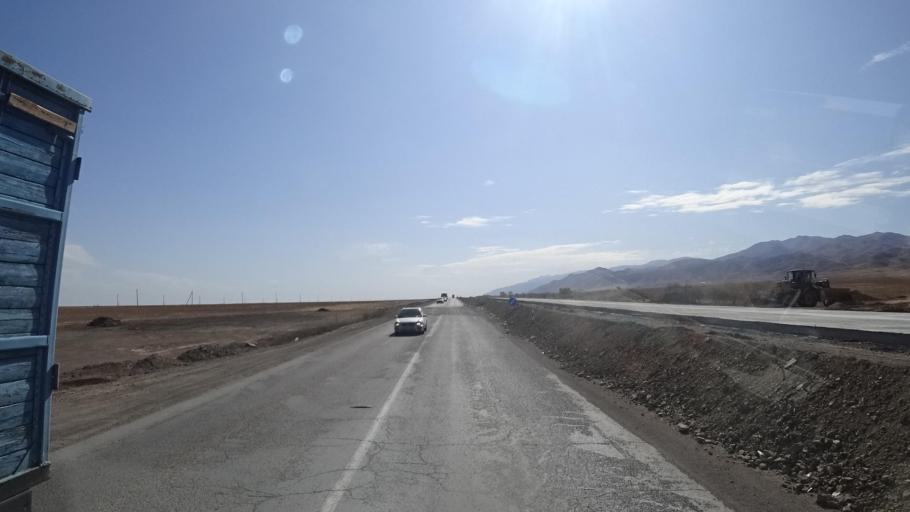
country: KG
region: Chuy
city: Ivanovka
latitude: 43.3994
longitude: 75.1171
